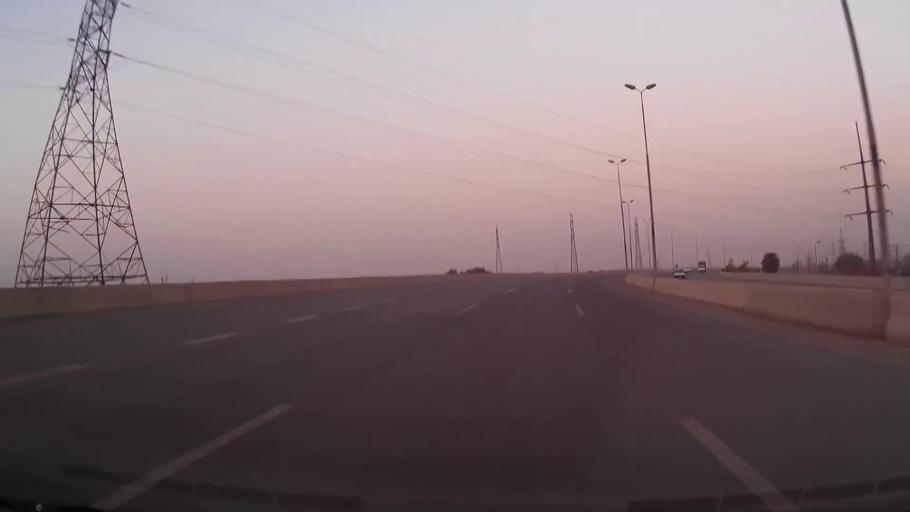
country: PK
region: Punjab
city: Lahore
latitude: 31.6099
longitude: 74.3100
